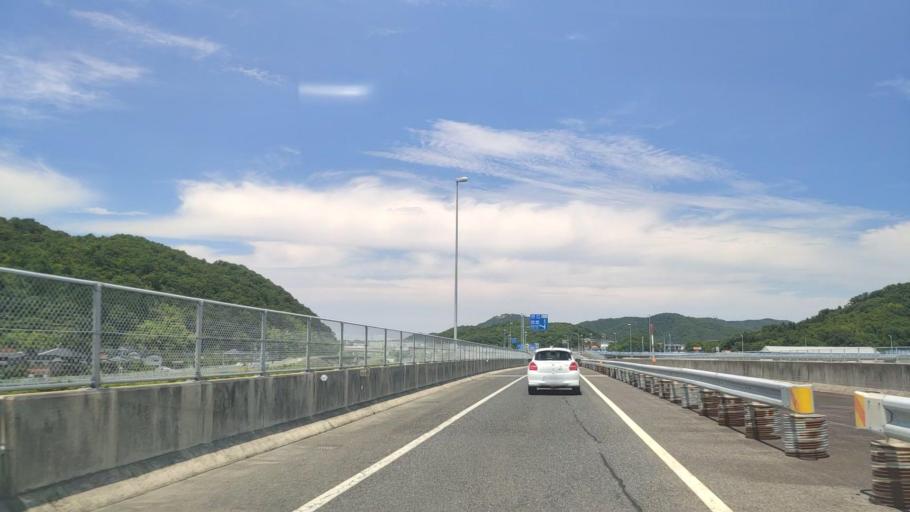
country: JP
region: Tottori
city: Tottori
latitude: 35.4654
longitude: 134.2430
